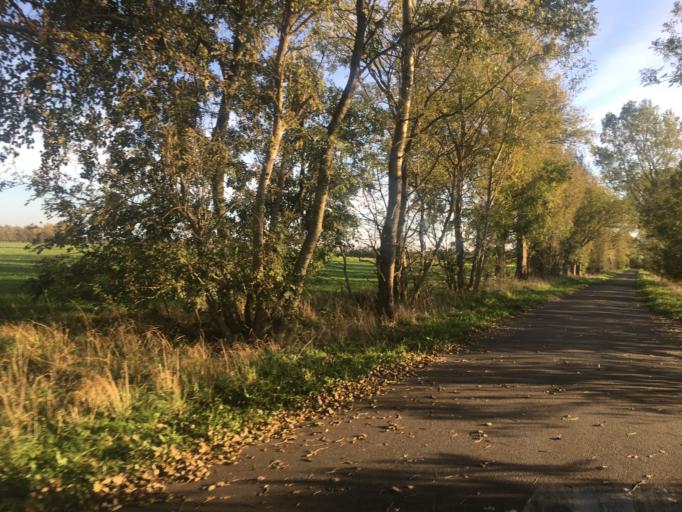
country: DE
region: Schleswig-Holstein
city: Bramstedtlund
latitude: 54.8661
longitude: 9.0805
